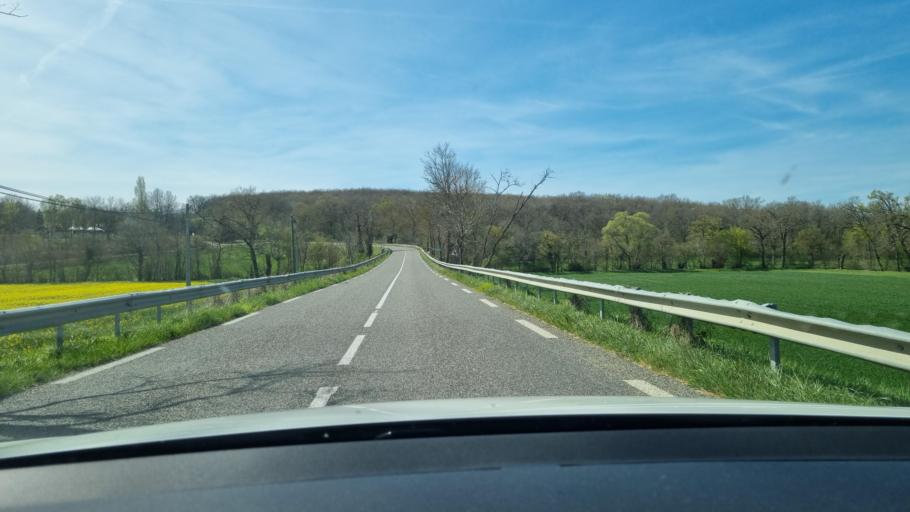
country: FR
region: Midi-Pyrenees
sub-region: Departement du Gers
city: Samatan
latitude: 43.4895
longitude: 1.0259
